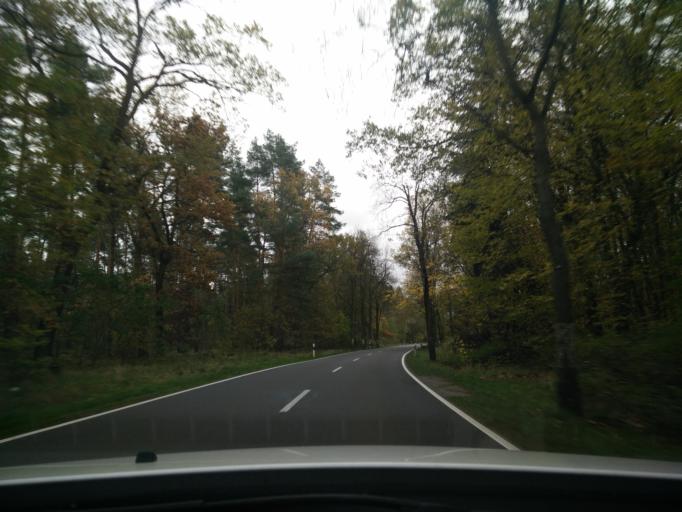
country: DE
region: Brandenburg
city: Nauen
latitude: 52.6284
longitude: 12.9368
